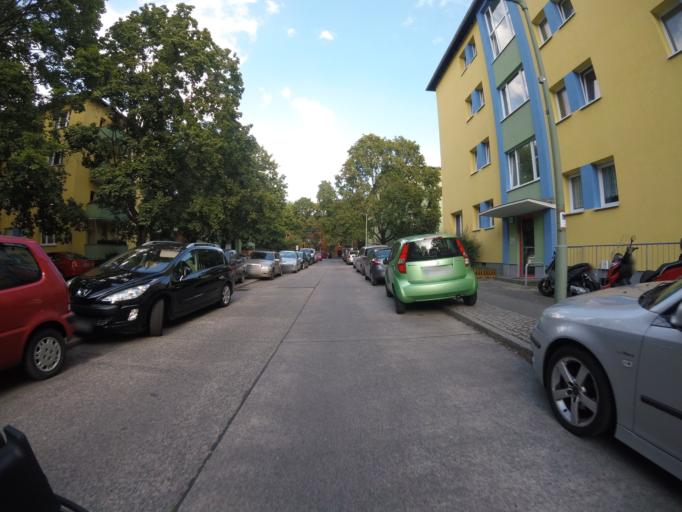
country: DE
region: Berlin
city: Charlottenburg-Nord
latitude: 52.5372
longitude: 13.2915
